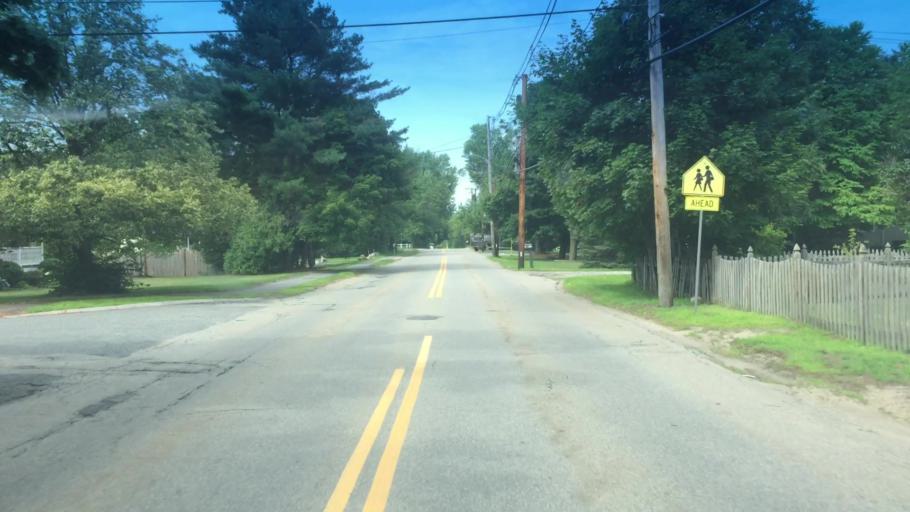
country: US
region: Massachusetts
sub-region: Norfolk County
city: Franklin
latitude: 42.1040
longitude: -71.3957
